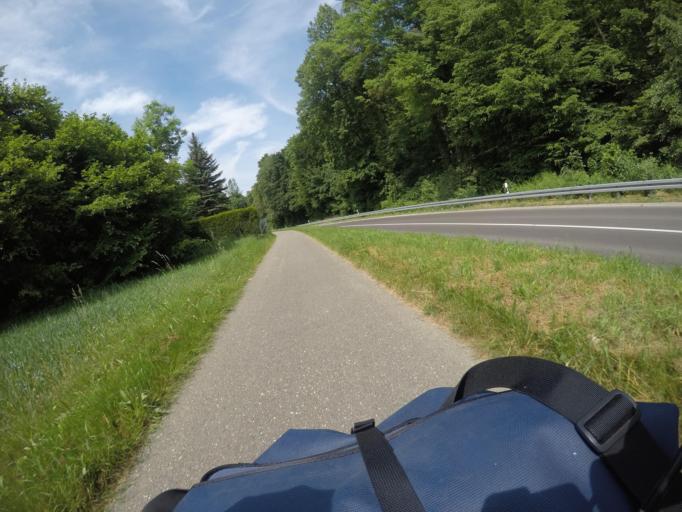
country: DE
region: Baden-Wuerttemberg
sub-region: Karlsruhe Region
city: Weingarten
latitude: 48.9834
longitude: 8.4960
